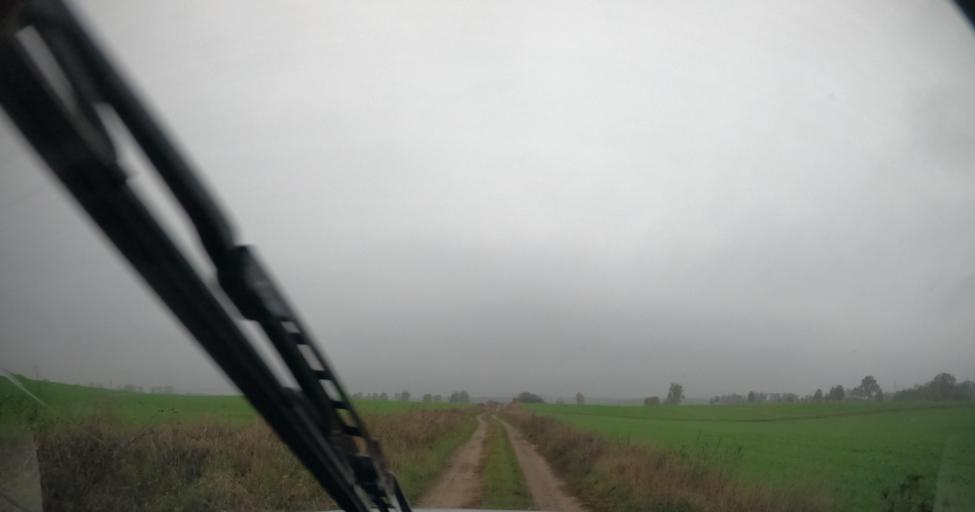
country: PL
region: West Pomeranian Voivodeship
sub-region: Powiat drawski
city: Drawsko Pomorskie
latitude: 53.5268
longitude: 15.7772
